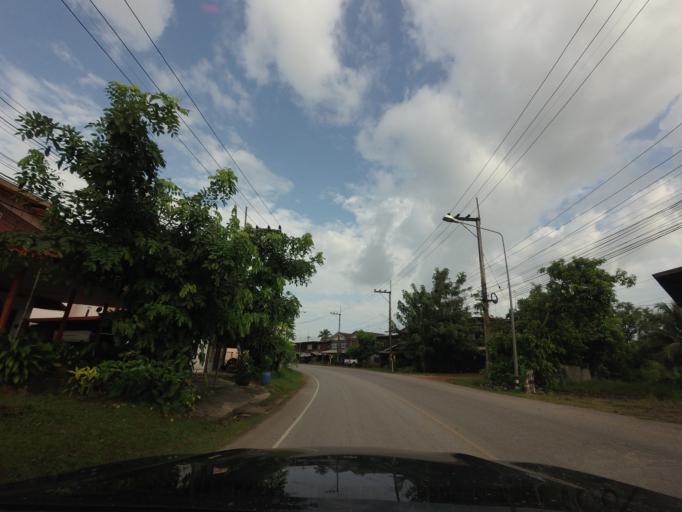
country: TH
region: Nong Khai
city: Pho Tak
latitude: 17.7795
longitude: 102.3943
